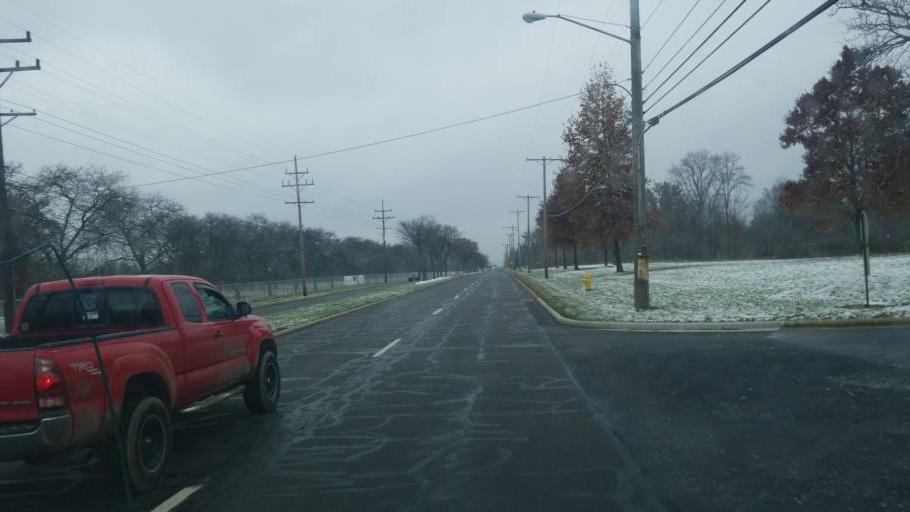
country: US
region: Ohio
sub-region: Cuyahoga County
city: Brecksville
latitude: 41.2921
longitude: -81.6270
